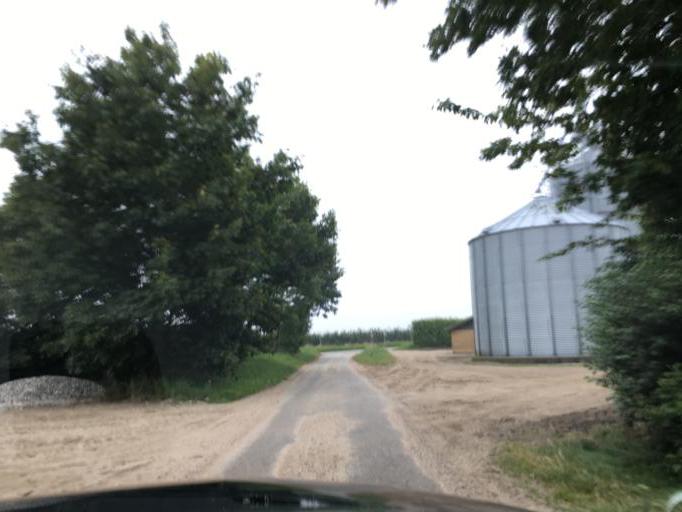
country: DK
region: South Denmark
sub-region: Kolding Kommune
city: Kolding
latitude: 55.5659
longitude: 9.4423
